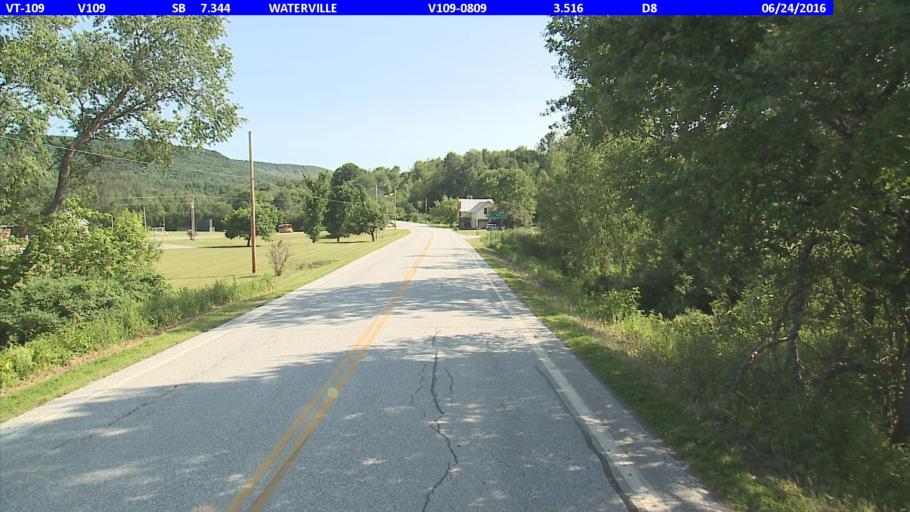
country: US
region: Vermont
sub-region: Lamoille County
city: Johnson
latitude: 44.7281
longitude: -72.7493
